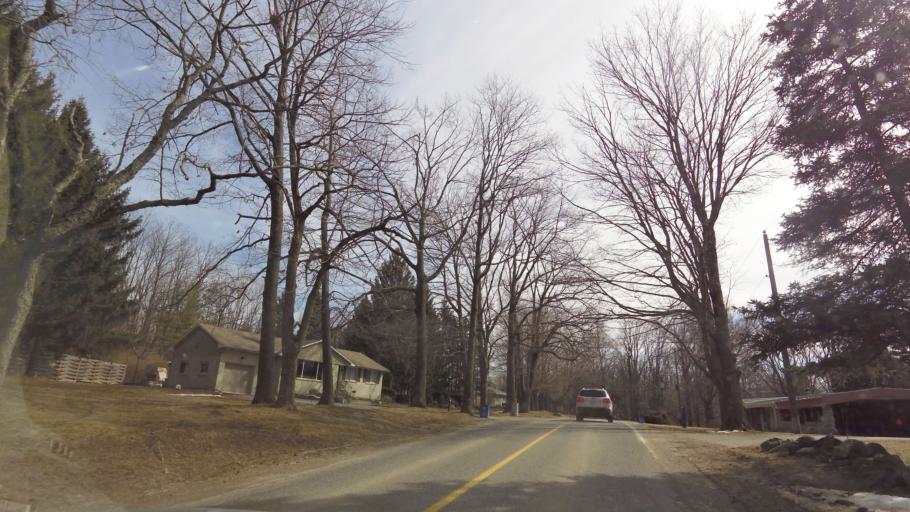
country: CA
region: Ontario
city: Burlington
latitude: 43.3669
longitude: -79.8828
